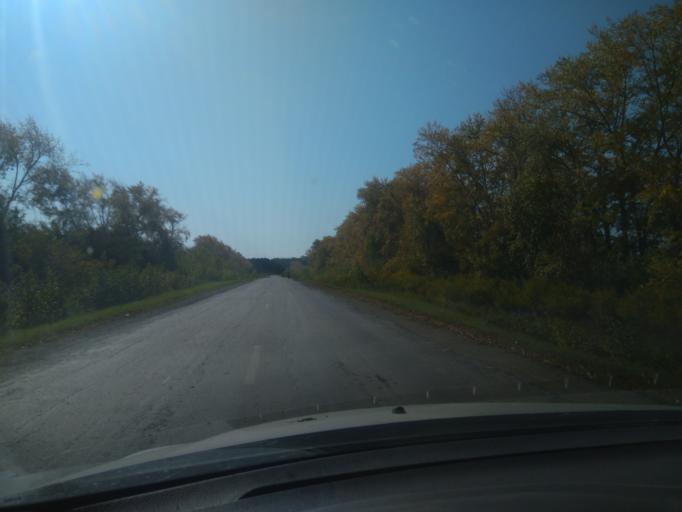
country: RU
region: Sverdlovsk
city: Pokrovskoye
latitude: 56.4585
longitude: 61.6085
